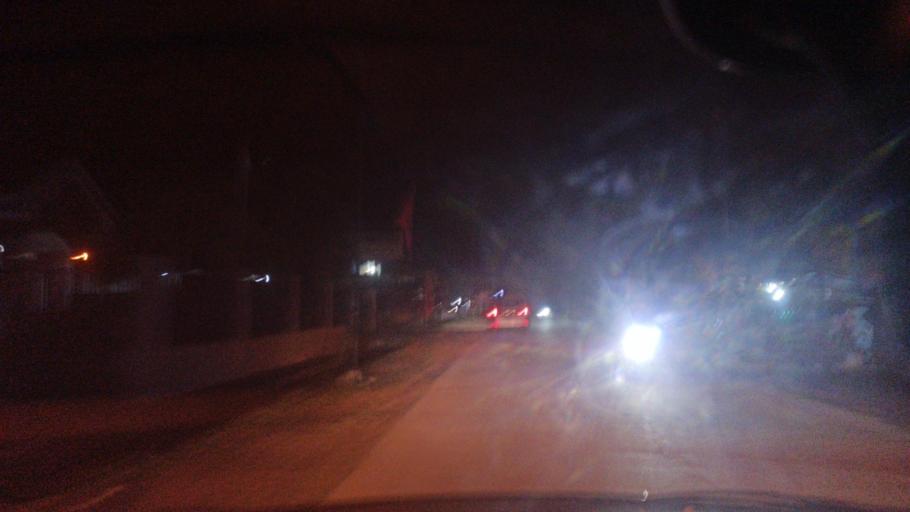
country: ID
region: South Sumatra
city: Palembang
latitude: -2.9201
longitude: 104.7993
